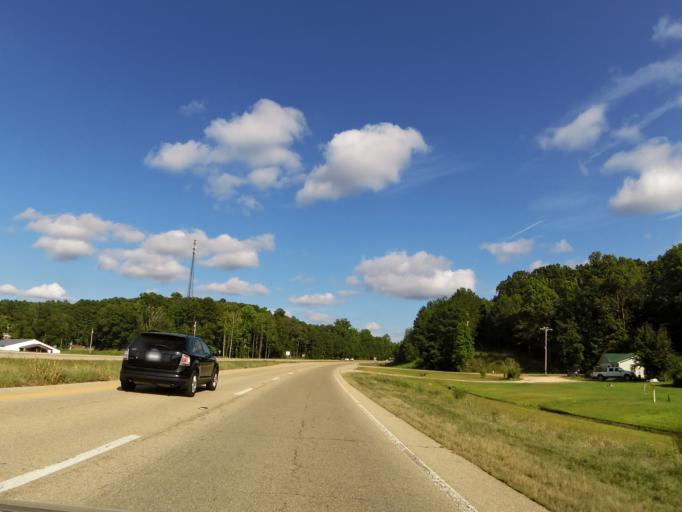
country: US
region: Mississippi
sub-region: Alcorn County
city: Farmington
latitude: 34.8507
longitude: -88.3425
